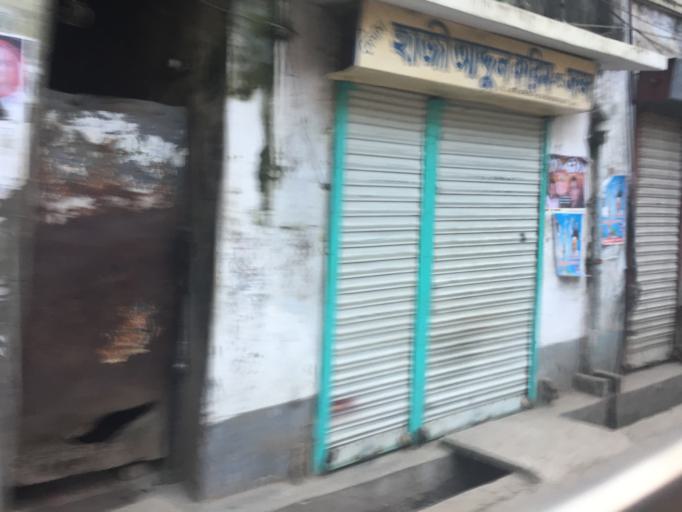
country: BD
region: Dhaka
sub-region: Dhaka
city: Dhaka
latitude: 23.7197
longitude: 90.4065
